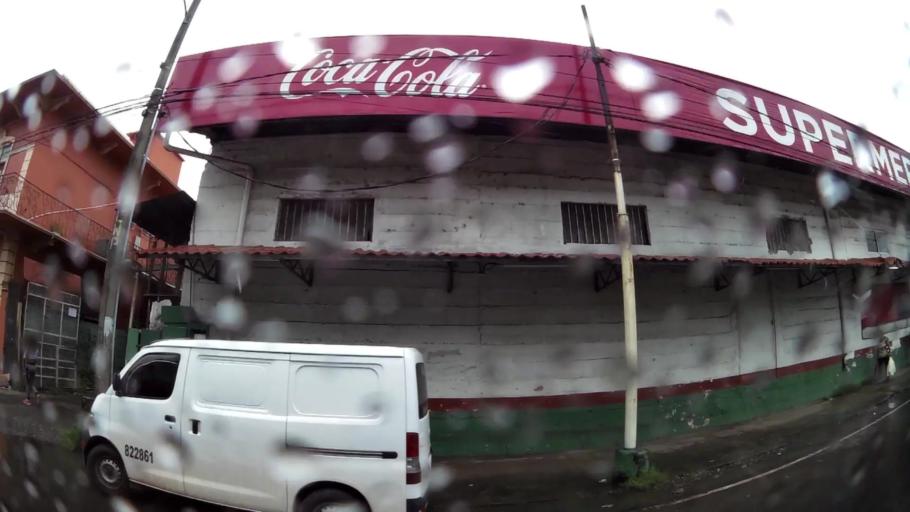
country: PA
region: Chiriqui
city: David
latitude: 8.4278
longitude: -82.4238
